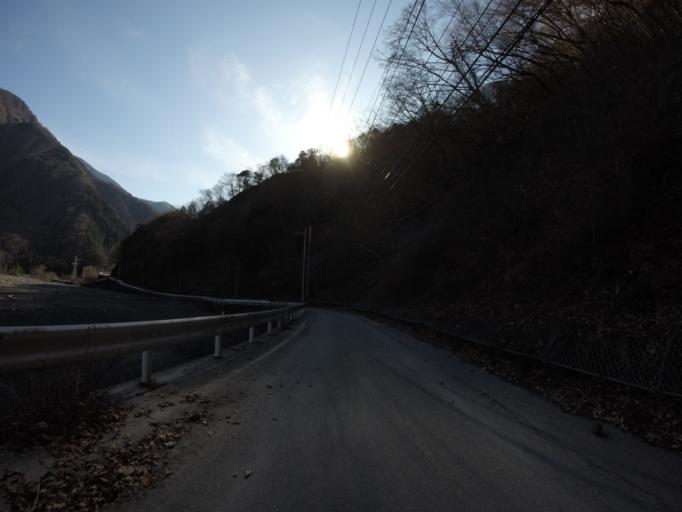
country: JP
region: Yamanashi
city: Ryuo
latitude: 35.4021
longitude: 138.3261
